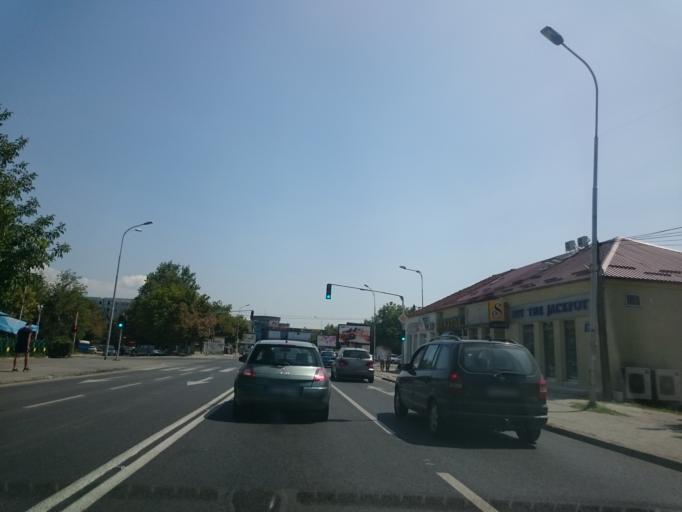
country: MK
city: Krushopek
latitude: 42.0067
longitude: 21.3617
